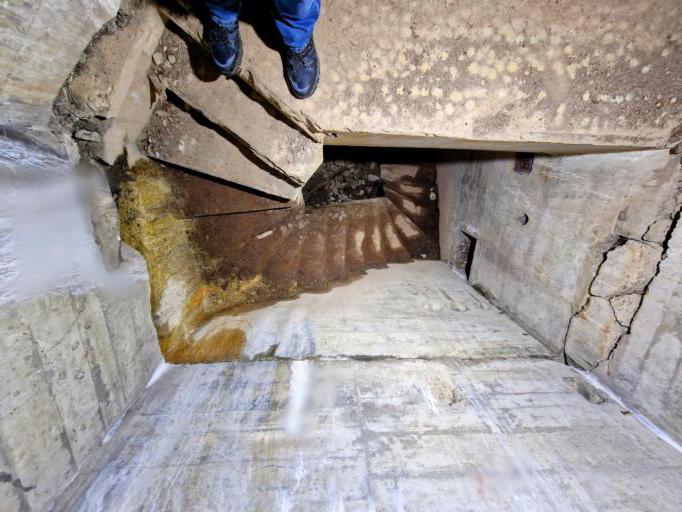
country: PL
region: Lubusz
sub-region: Powiat swiebodzinski
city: Lubrza
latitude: 52.3477
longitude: 15.4807
